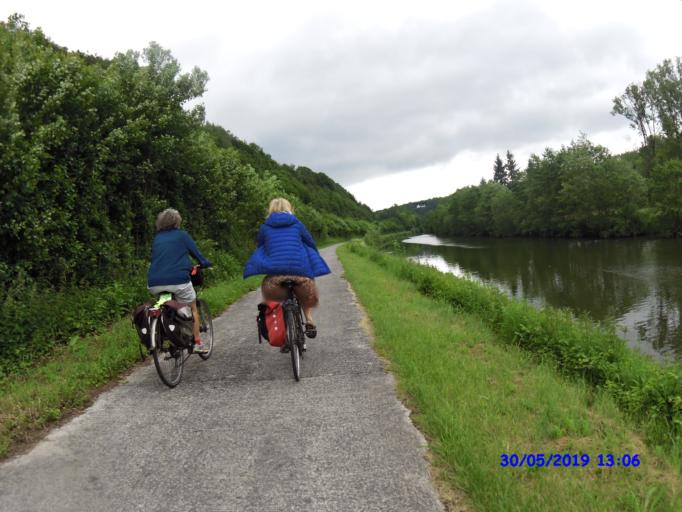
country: BE
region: Wallonia
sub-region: Province du Hainaut
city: Thuin
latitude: 50.3520
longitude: 4.3083
